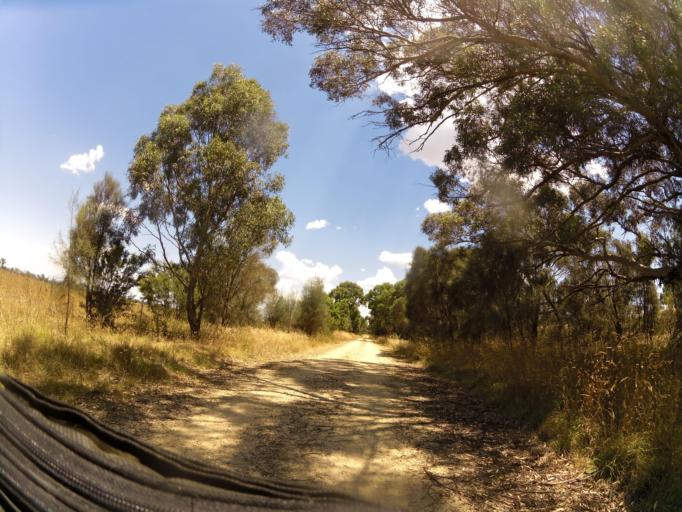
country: AU
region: Victoria
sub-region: Wellington
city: Heyfield
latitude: -37.9793
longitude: 146.8479
